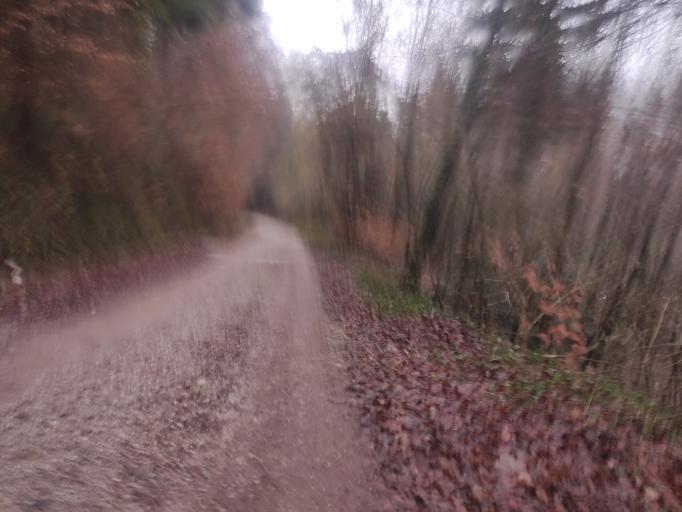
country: AT
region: Salzburg
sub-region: Politischer Bezirk Salzburg-Umgebung
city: Mattsee
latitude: 47.9698
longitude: 13.1178
